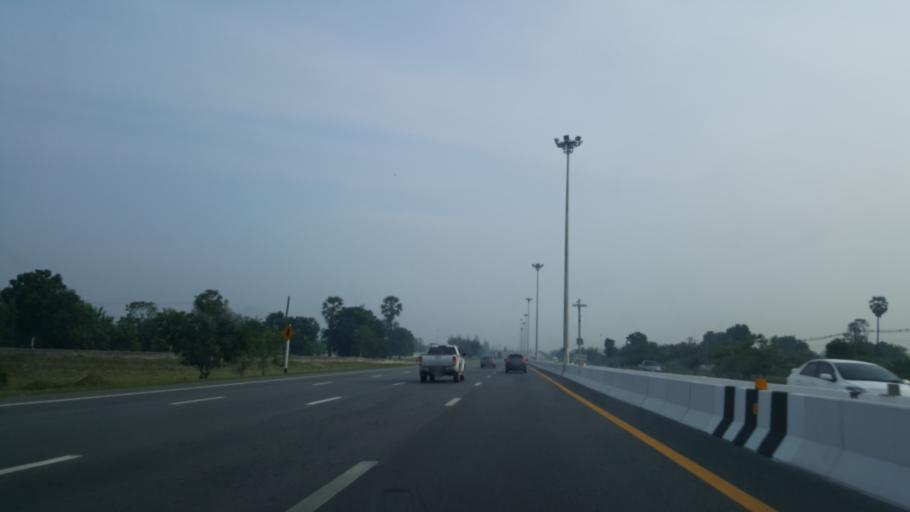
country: TH
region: Chon Buri
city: Chon Buri
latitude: 13.3399
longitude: 101.0250
